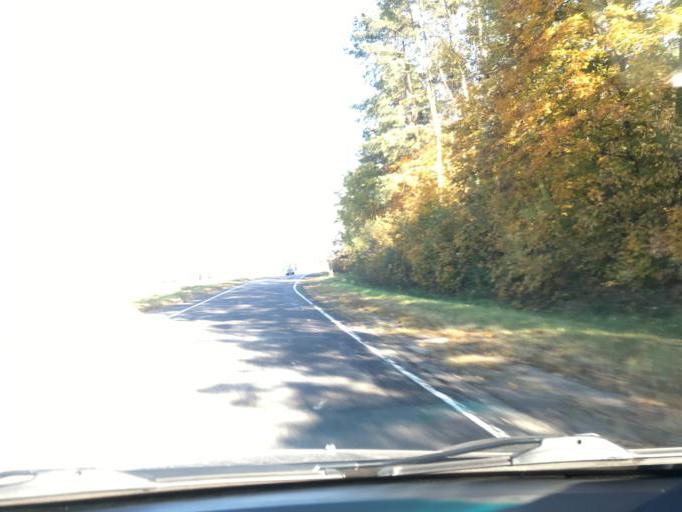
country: BY
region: Gomel
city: Gomel
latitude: 52.3836
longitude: 30.8278
